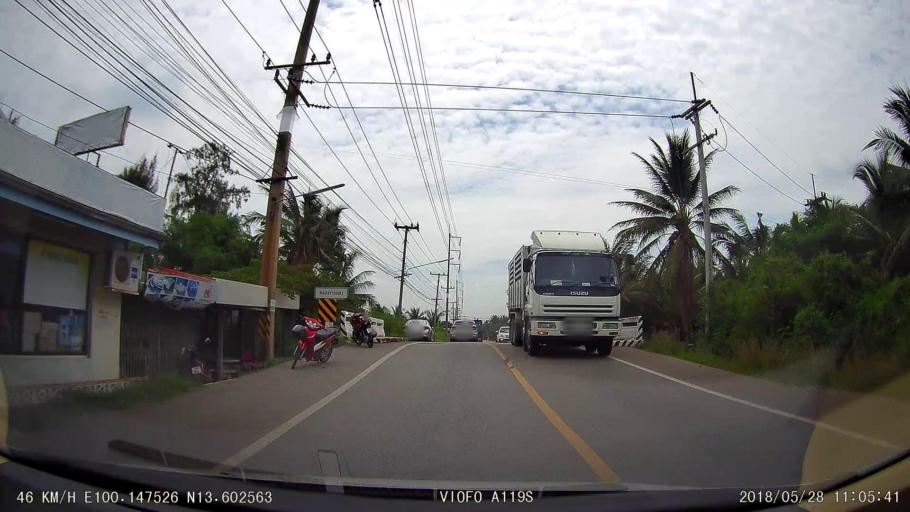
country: TH
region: Samut Sakhon
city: Ban Phaeo
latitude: 13.6026
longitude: 100.1476
